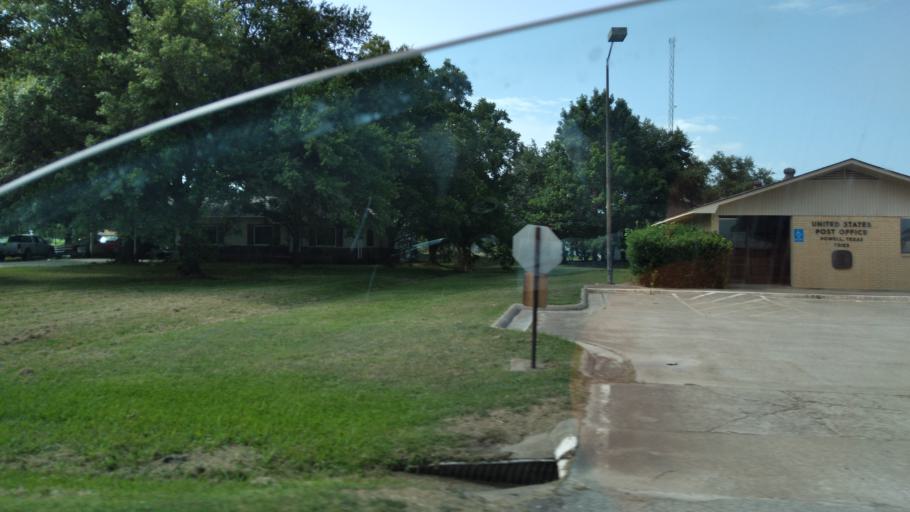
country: US
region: Texas
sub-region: Navarro County
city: Kerens
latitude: 32.1175
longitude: -96.3279
